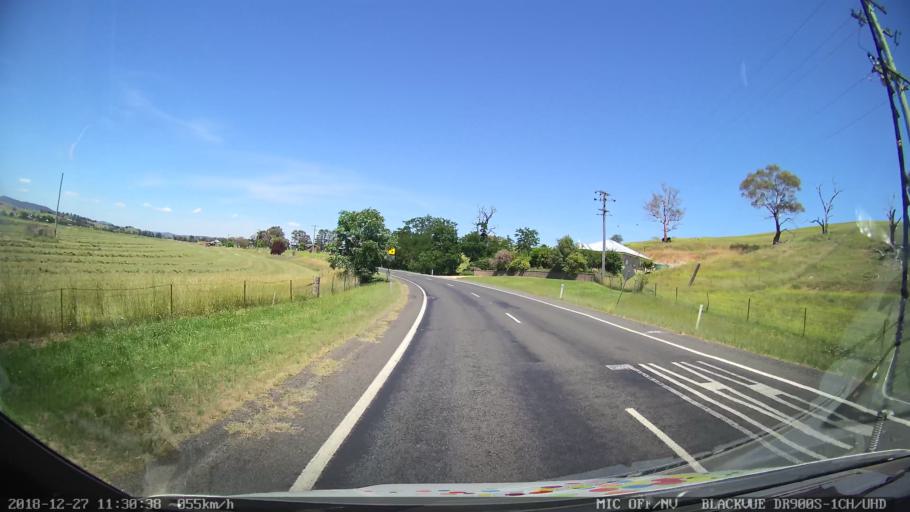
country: AU
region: New South Wales
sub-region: Bathurst Regional
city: Perthville
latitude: -33.4882
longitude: 149.5440
